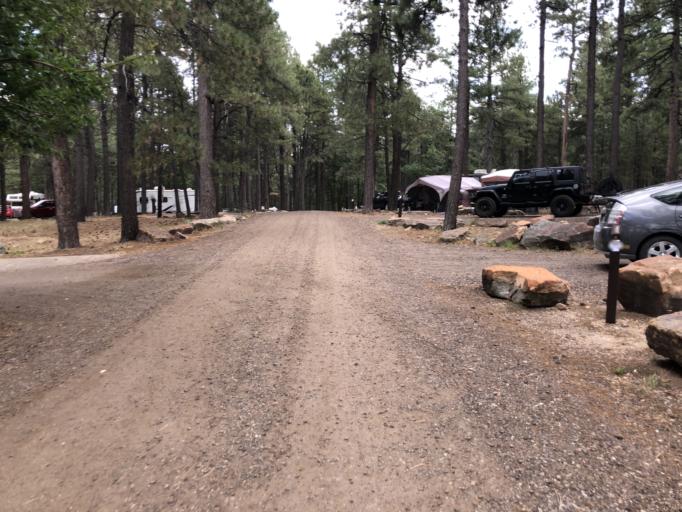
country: US
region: Arizona
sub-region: Gila County
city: Star Valley
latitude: 34.3330
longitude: -110.9385
